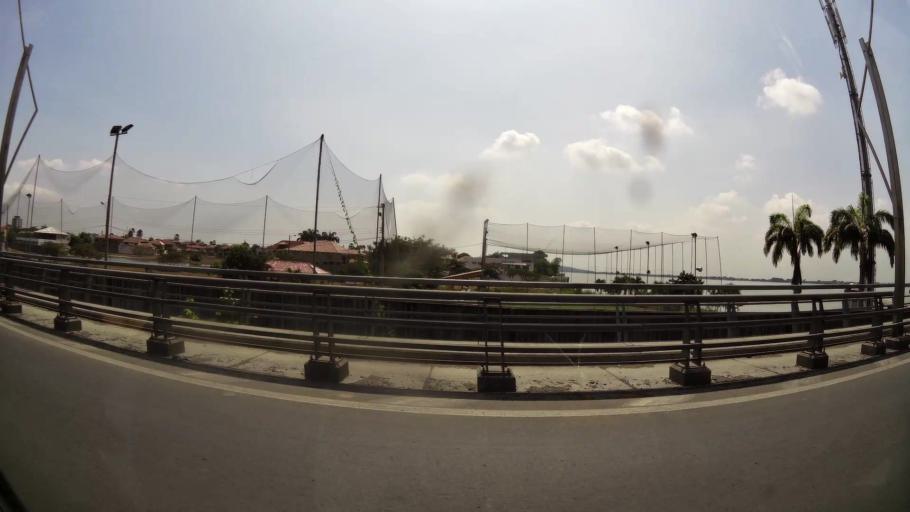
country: EC
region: Guayas
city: Eloy Alfaro
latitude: -2.1539
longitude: -79.8617
